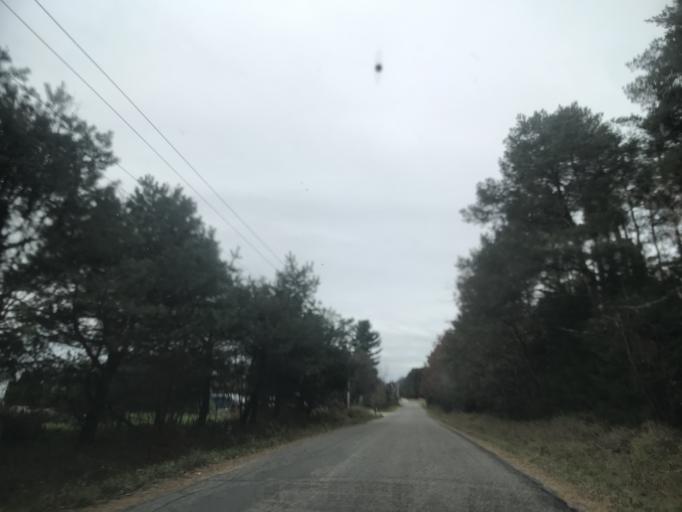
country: US
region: Wisconsin
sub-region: Menominee County
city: Legend Lake
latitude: 45.1795
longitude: -88.4552
